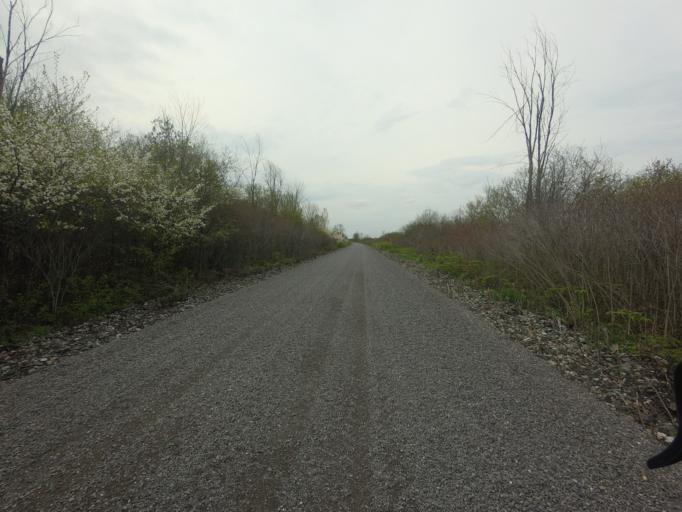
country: CA
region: Ontario
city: Carleton Place
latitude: 45.2014
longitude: -76.1680
